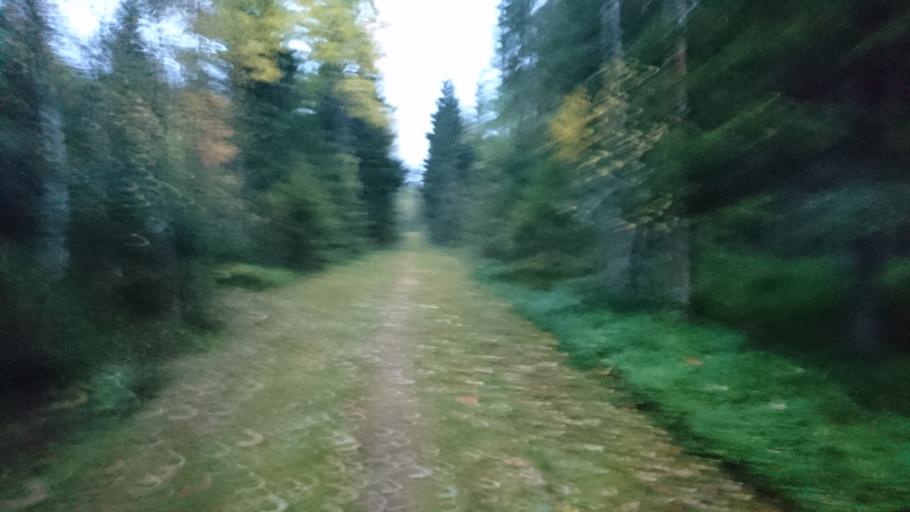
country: SE
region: Vaesterbotten
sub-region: Robertsfors Kommun
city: Robertsfors
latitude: 64.2300
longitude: 20.9962
